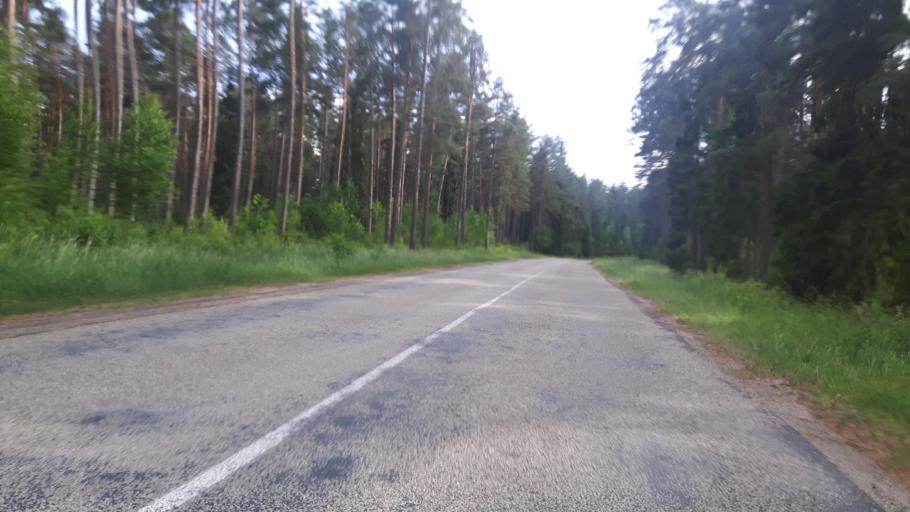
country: LV
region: Engure
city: Smarde
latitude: 57.0032
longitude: 23.3319
